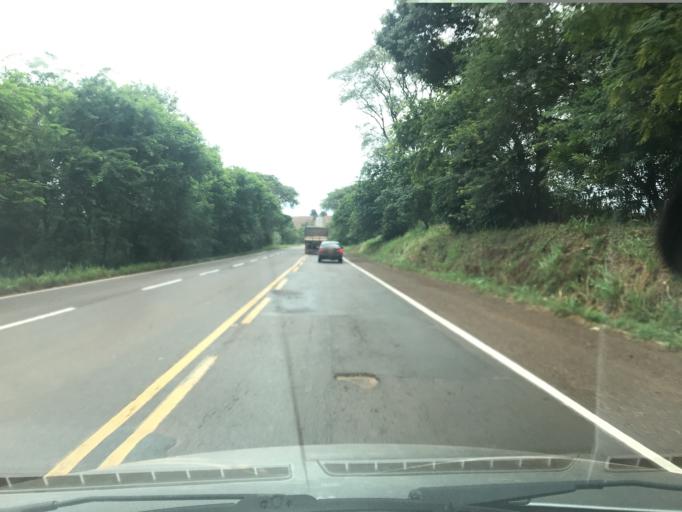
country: BR
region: Parana
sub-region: Terra Boa
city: Terra Boa
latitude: -23.6184
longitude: -52.4354
